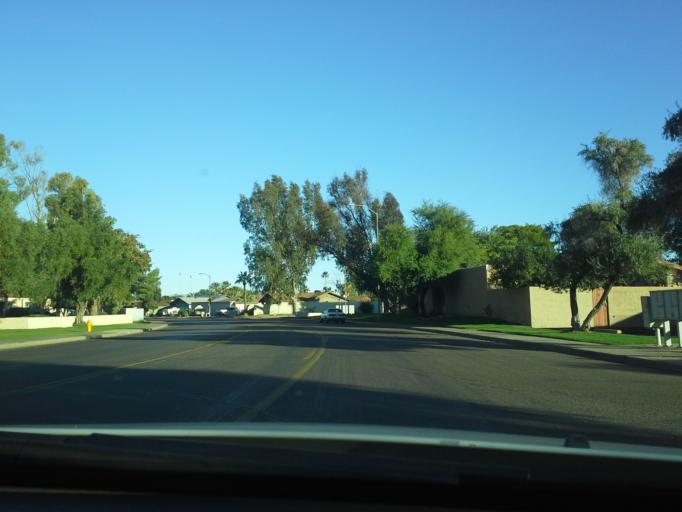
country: US
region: Arizona
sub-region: Maricopa County
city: Tempe
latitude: 33.4260
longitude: -111.8786
